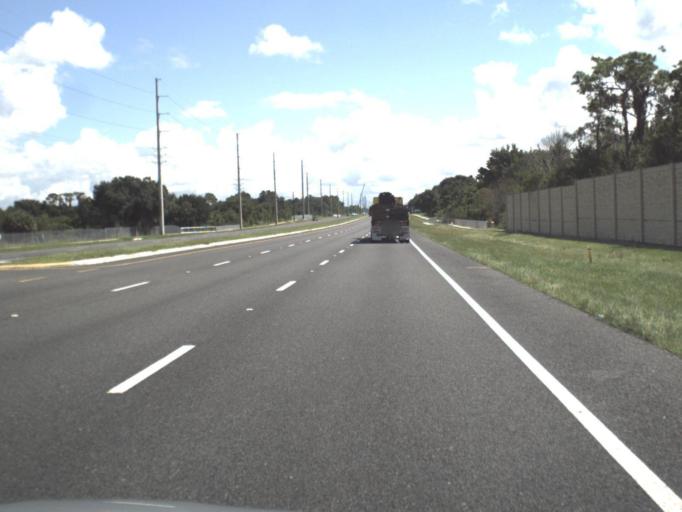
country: US
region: Florida
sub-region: Sarasota County
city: The Meadows
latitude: 27.4318
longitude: -82.4121
